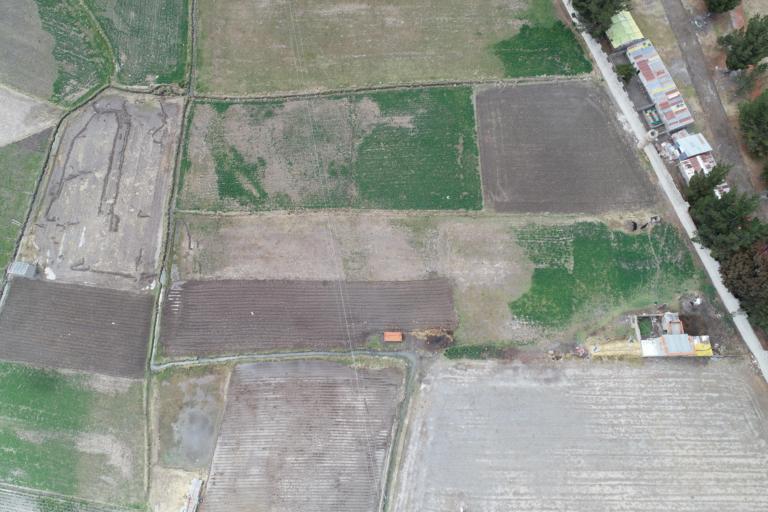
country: BO
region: La Paz
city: Achacachi
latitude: -16.0319
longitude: -68.6864
